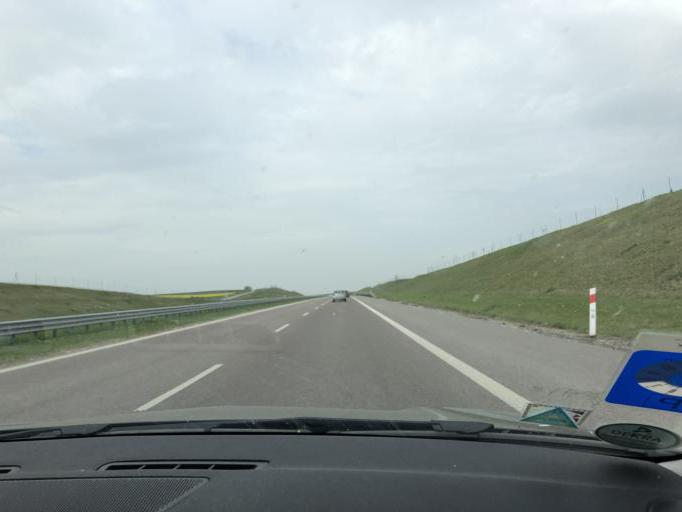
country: PL
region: Subcarpathian Voivodeship
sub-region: Powiat jaroslawski
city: Wierzbna
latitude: 50.0037
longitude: 22.6002
